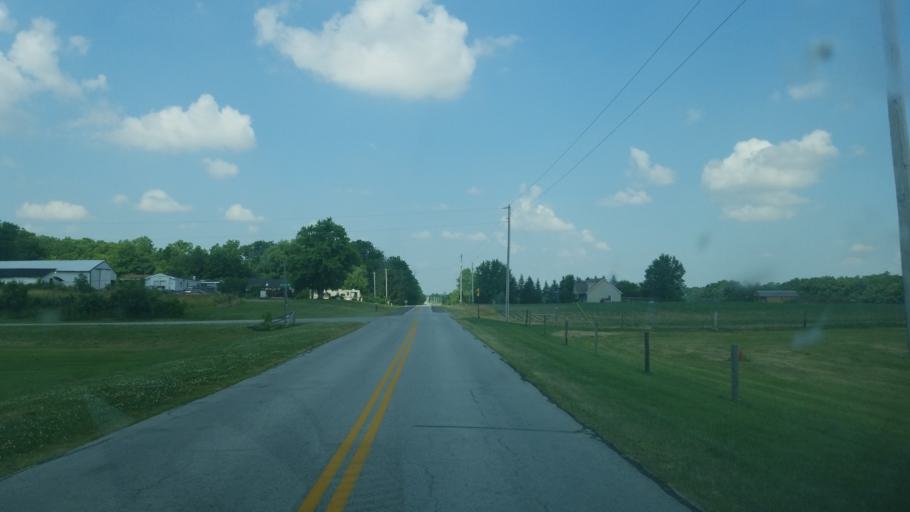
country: US
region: Ohio
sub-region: Auglaize County
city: Cridersville
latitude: 40.5714
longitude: -84.0600
